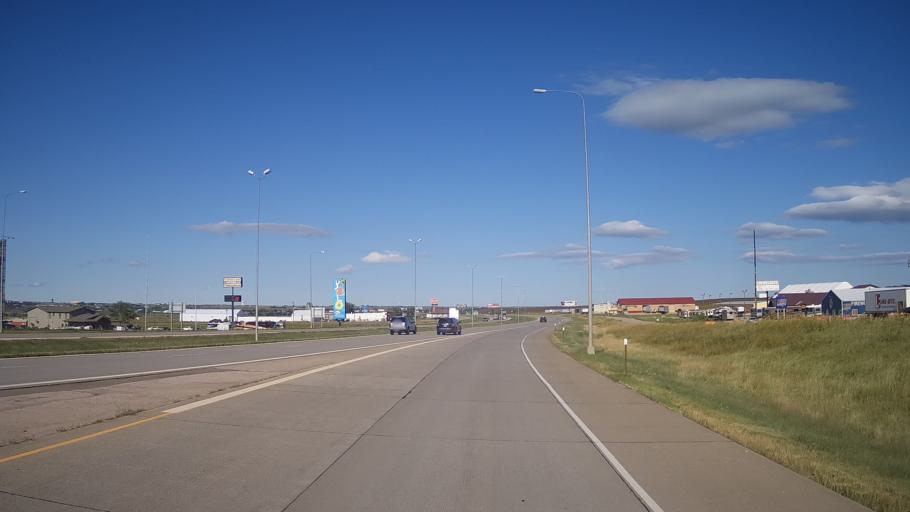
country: US
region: South Dakota
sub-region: Pennington County
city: Rapid Valley
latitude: 44.0993
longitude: -103.1463
